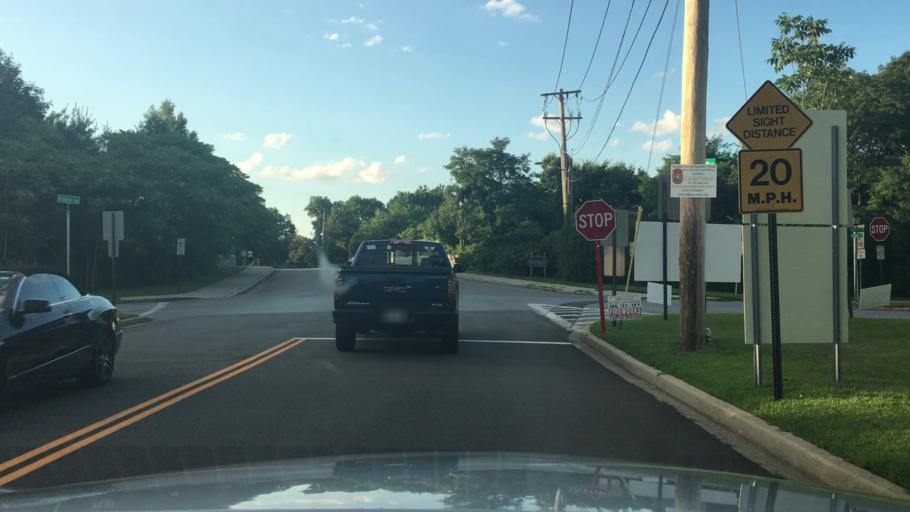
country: US
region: New York
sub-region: Nassau County
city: Carle Place
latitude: 40.7580
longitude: -73.6048
